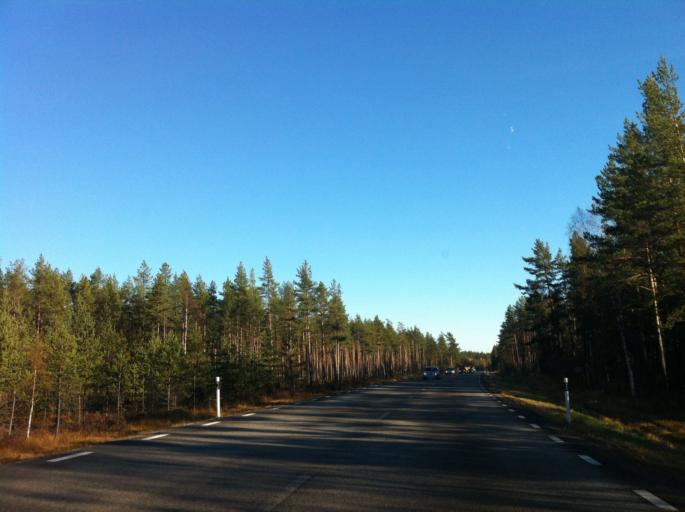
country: SE
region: Dalarna
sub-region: Leksand Municipality
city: Siljansnas
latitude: 60.9168
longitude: 14.8751
